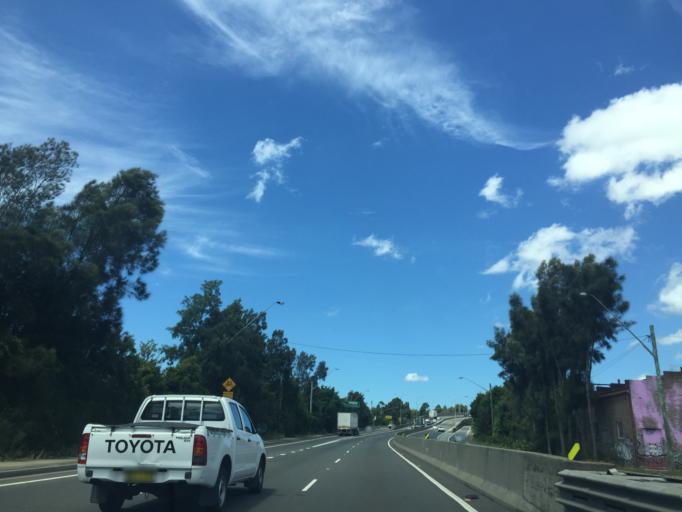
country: AU
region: New South Wales
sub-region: Strathfield
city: Strathfield South
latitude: -33.8814
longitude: 151.0691
